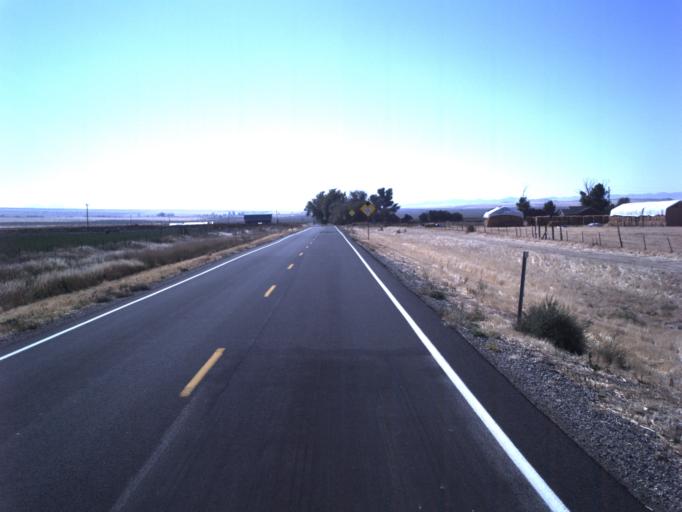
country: US
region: Utah
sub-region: Tooele County
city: Grantsville
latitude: 40.4982
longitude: -112.7481
